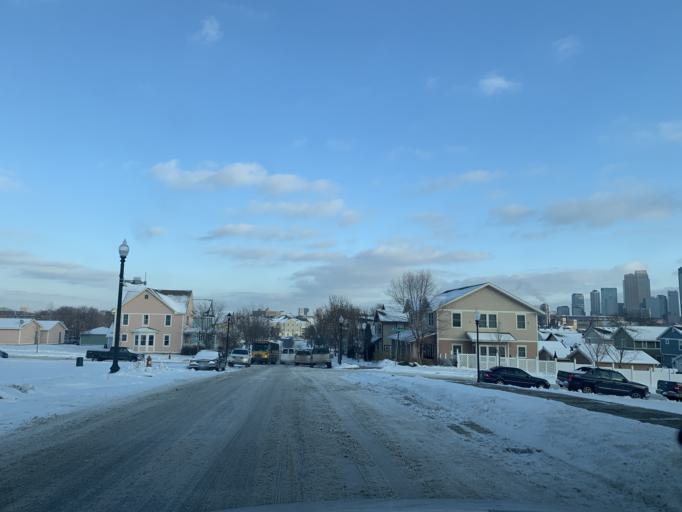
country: US
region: Minnesota
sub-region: Hennepin County
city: Minneapolis
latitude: 44.9890
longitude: -93.2962
